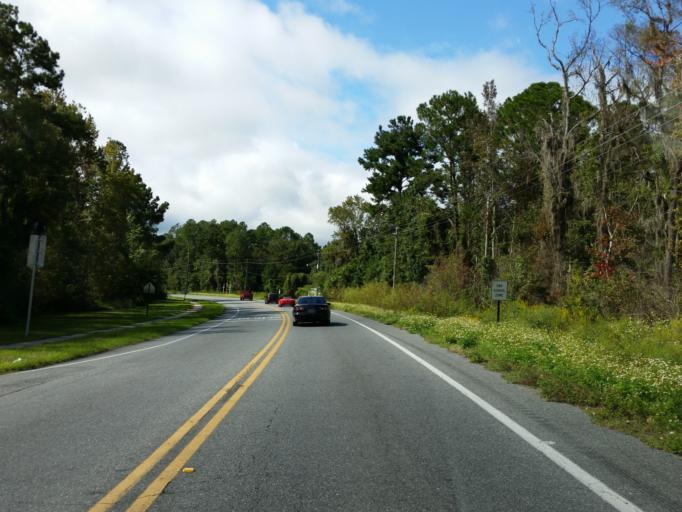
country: US
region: Florida
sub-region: Columbia County
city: Five Points
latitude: 30.2020
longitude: -82.6277
